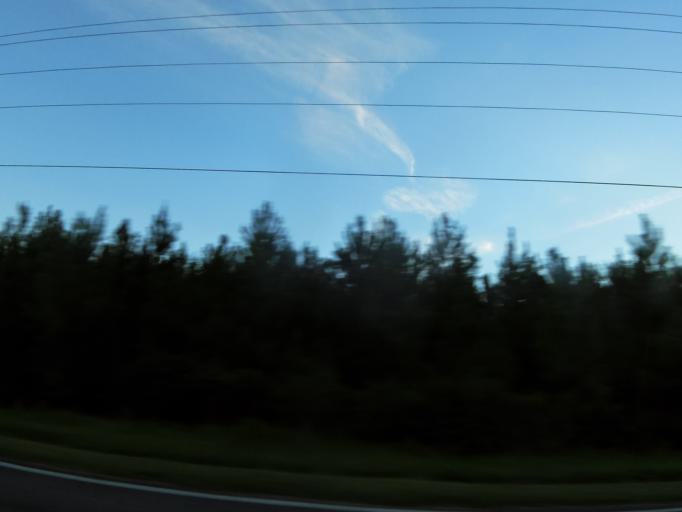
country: US
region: Georgia
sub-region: Camden County
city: Kingsland
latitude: 30.7724
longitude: -81.6968
